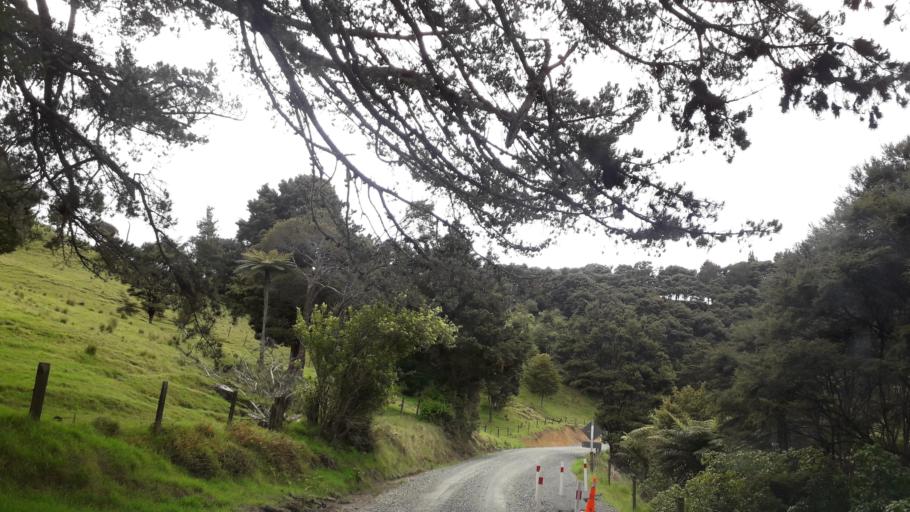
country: NZ
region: Northland
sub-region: Far North District
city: Taipa
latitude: -35.0542
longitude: 173.5558
